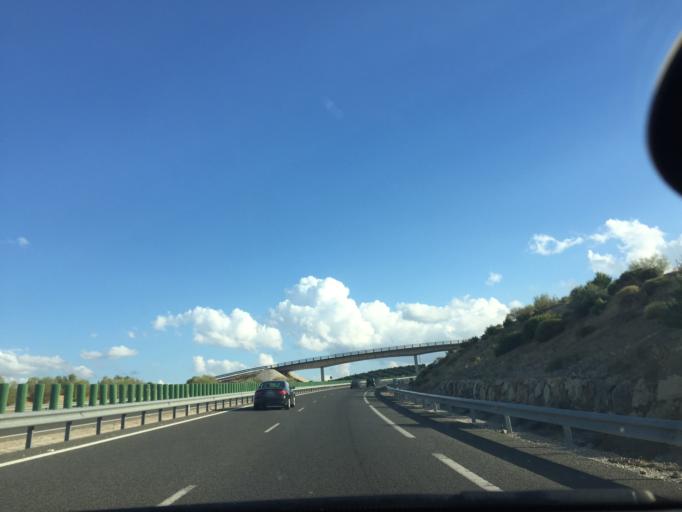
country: ES
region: Andalusia
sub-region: Provincia de Jaen
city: Jaen
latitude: 37.8152
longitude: -3.7367
